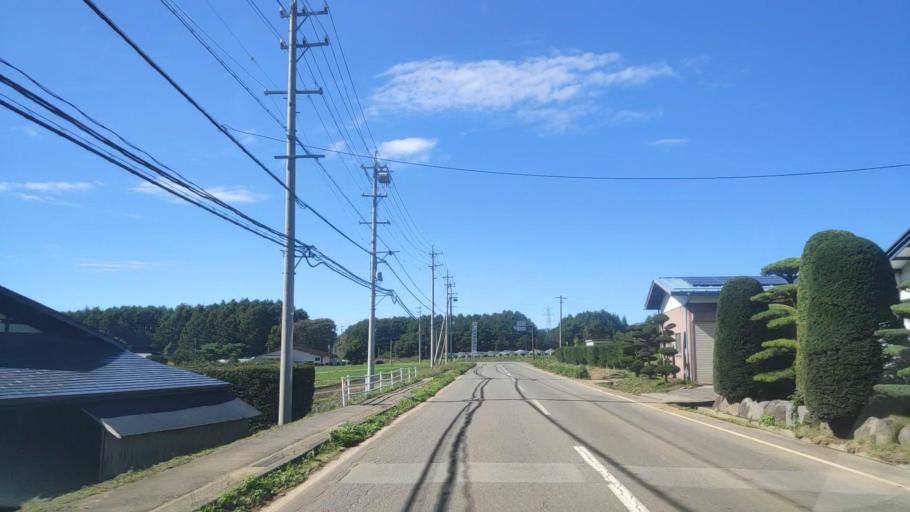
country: JP
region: Nagano
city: Chino
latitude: 35.9447
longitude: 138.2207
